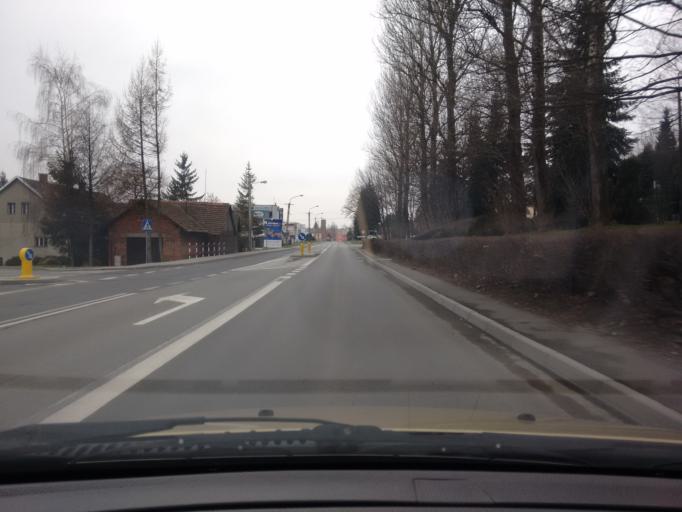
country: PL
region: Silesian Voivodeship
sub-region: Powiat cieszynski
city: Cieszyn
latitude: 49.7523
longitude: 18.6559
